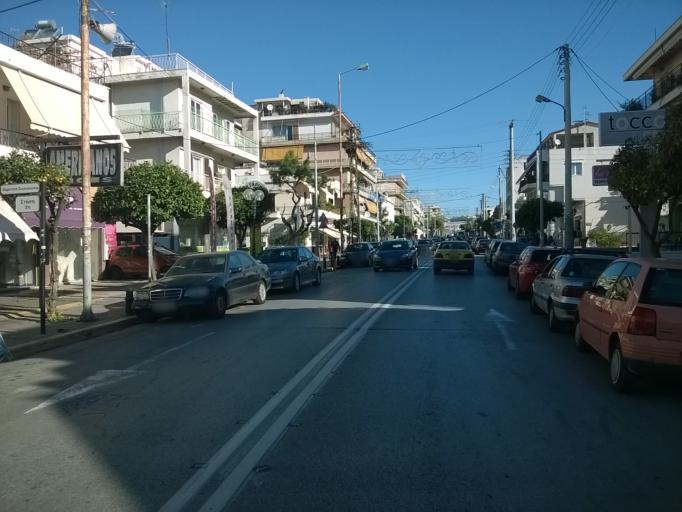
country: GR
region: Attica
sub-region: Nomarchia Athinas
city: Dhafni
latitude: 37.9436
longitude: 23.7333
